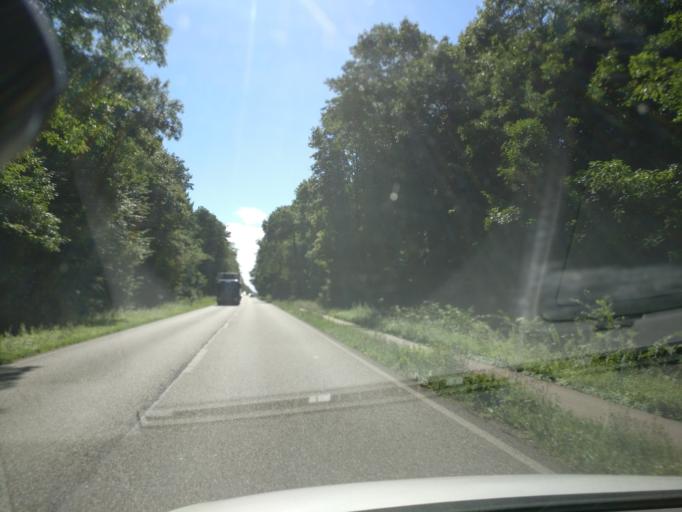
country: DE
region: Baden-Wuerttemberg
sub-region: Karlsruhe Region
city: Malsch
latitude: 48.9154
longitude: 8.3429
